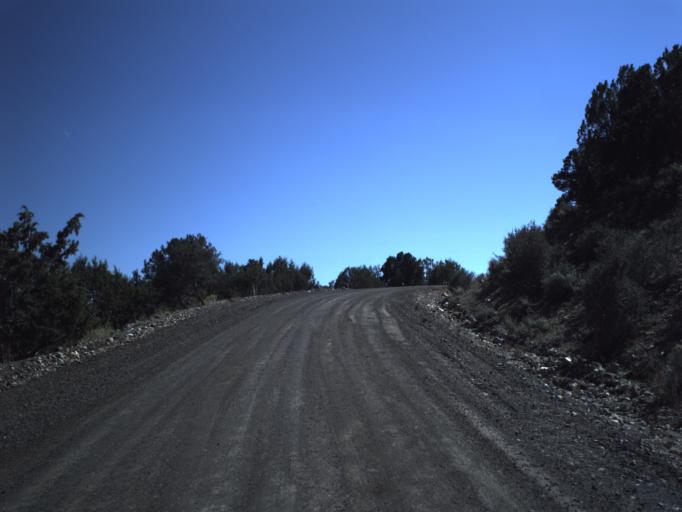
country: US
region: Utah
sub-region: Piute County
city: Junction
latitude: 38.2570
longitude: -112.3076
